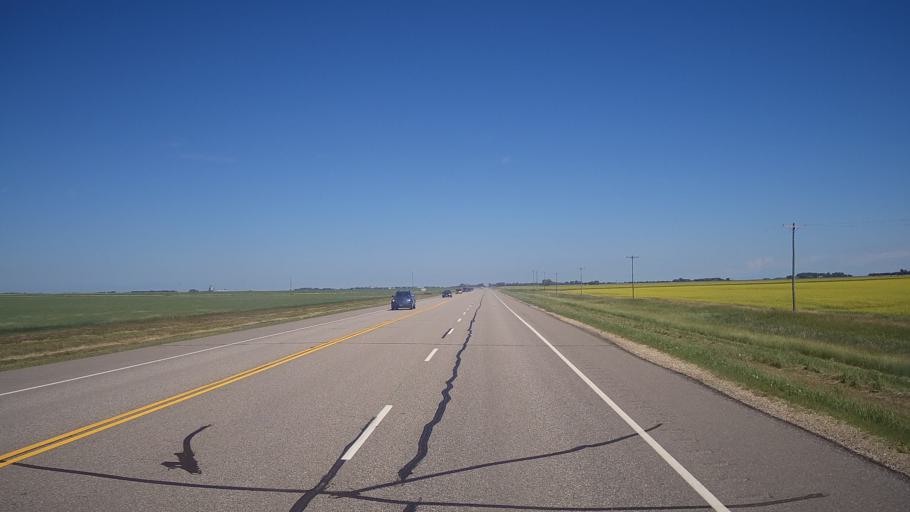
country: CA
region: Manitoba
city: Portage la Prairie
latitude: 50.0156
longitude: -98.4687
